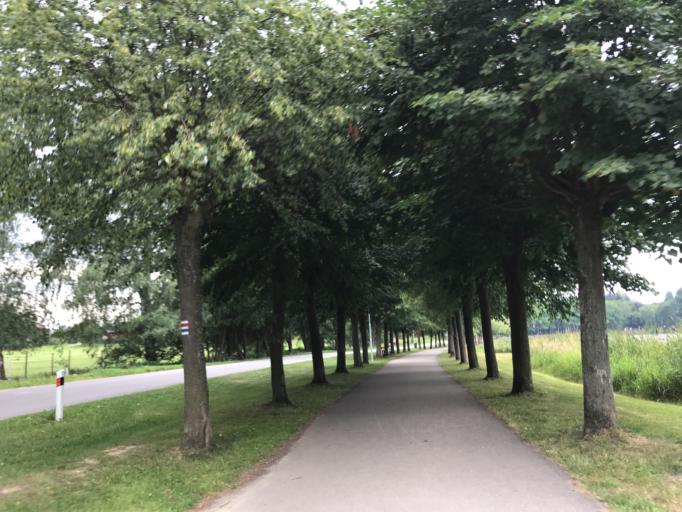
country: CZ
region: Jihocesky
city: Chlum u Trebone
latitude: 48.9589
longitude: 14.9393
